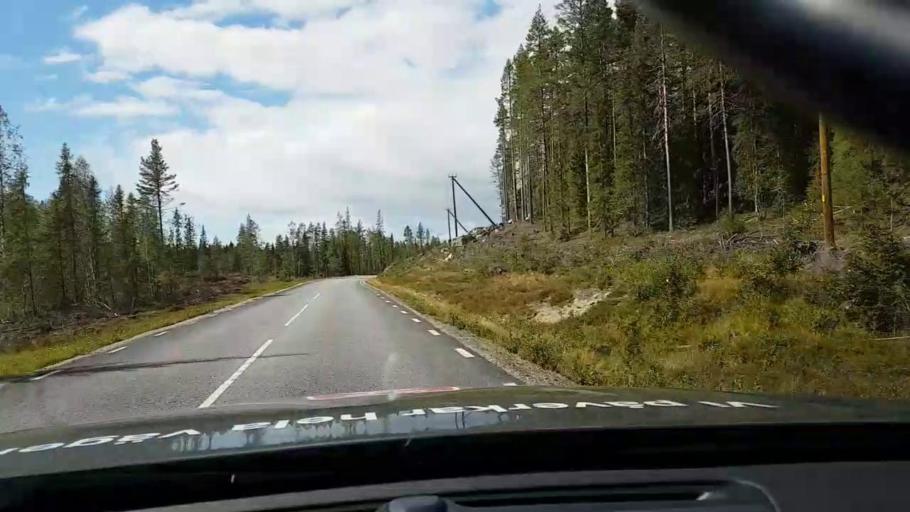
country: SE
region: Vaesterbotten
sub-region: Asele Kommun
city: Asele
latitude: 63.8450
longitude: 17.4212
